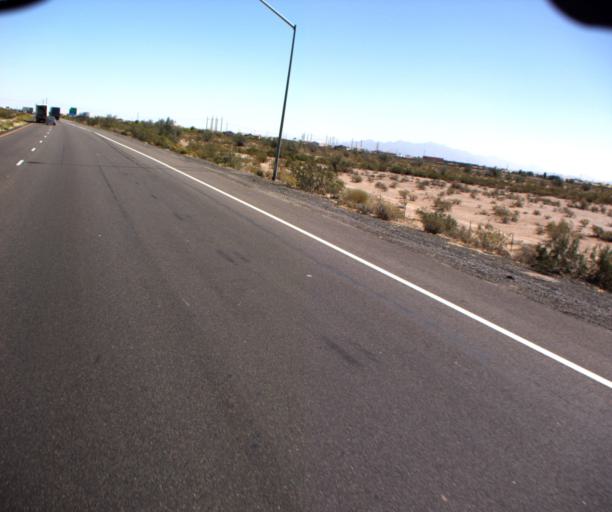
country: US
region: Arizona
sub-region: Maricopa County
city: Buckeye
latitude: 33.4269
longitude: -112.6159
